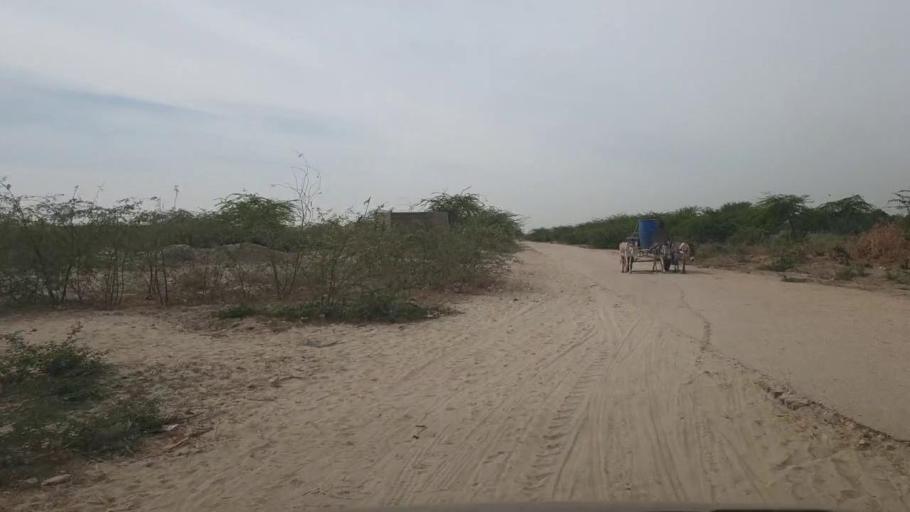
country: PK
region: Sindh
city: Umarkot
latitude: 25.2522
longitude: 69.7209
